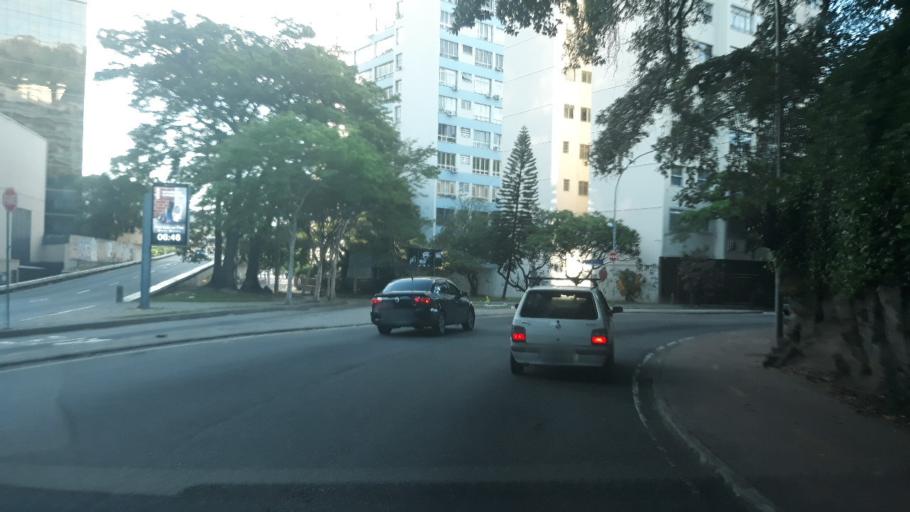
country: BR
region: Rio de Janeiro
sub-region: Rio De Janeiro
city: Rio de Janeiro
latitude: -22.9419
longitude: -43.1824
